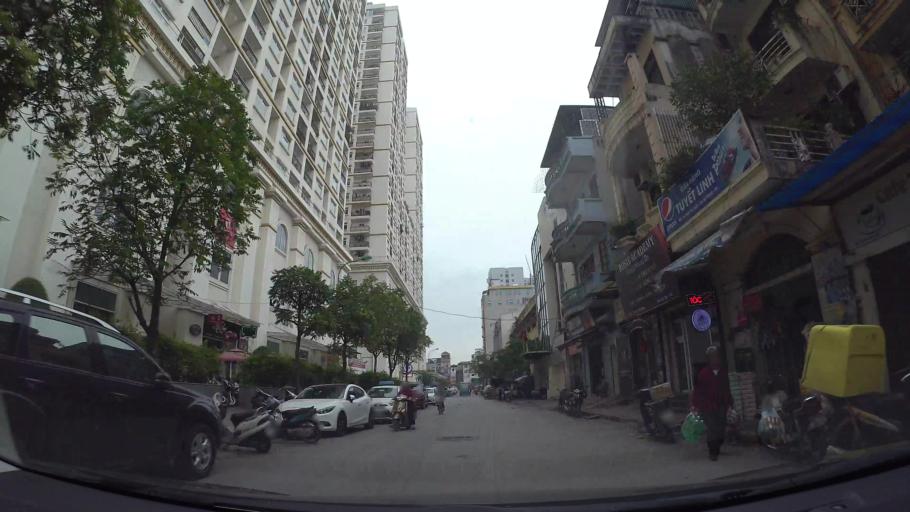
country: VN
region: Ha Noi
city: Hai BaTrung
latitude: 21.0006
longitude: 105.8692
